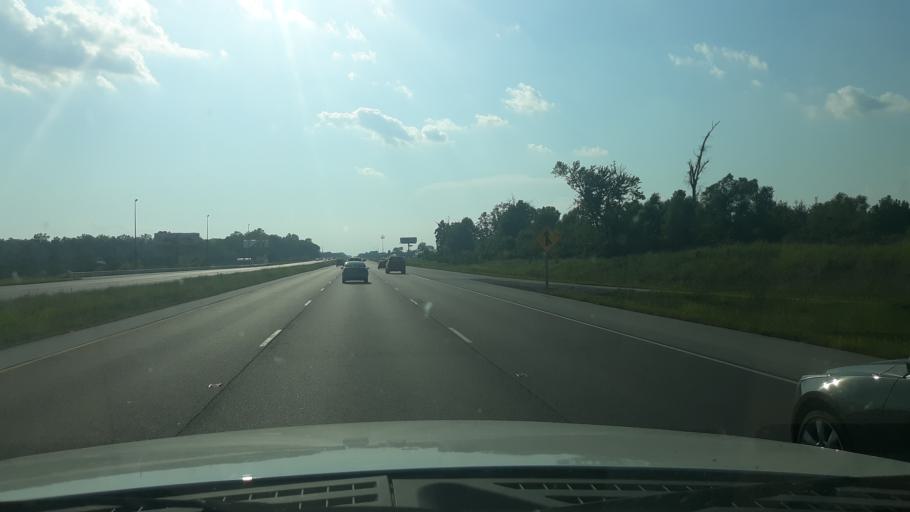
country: US
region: Illinois
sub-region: Williamson County
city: Crainville
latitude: 37.7452
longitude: -89.0613
